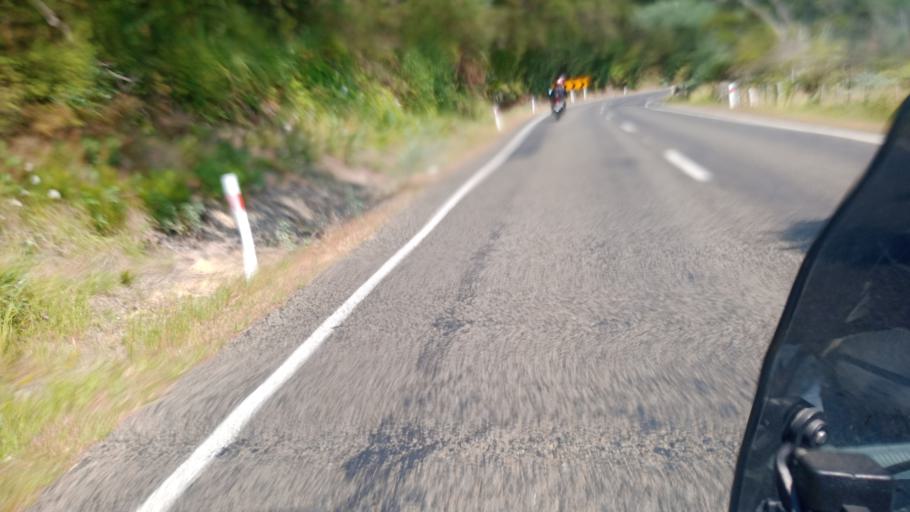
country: NZ
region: Bay of Plenty
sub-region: Opotiki District
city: Opotiki
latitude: -37.5916
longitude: 178.2379
